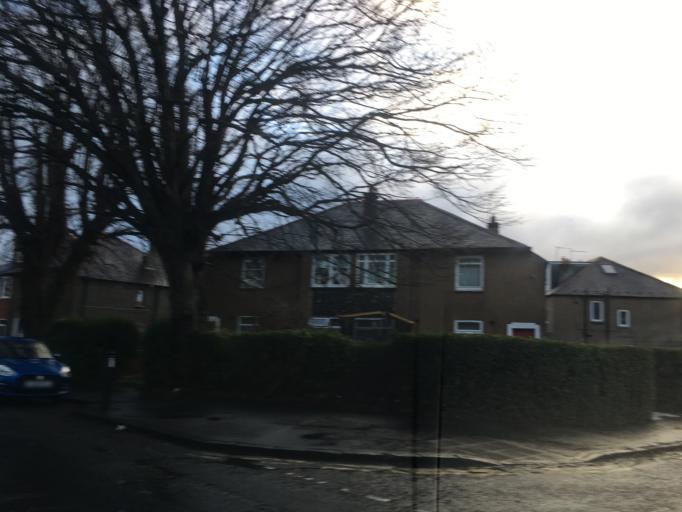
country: GB
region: Scotland
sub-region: Edinburgh
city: Colinton
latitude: 55.9357
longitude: -3.2787
